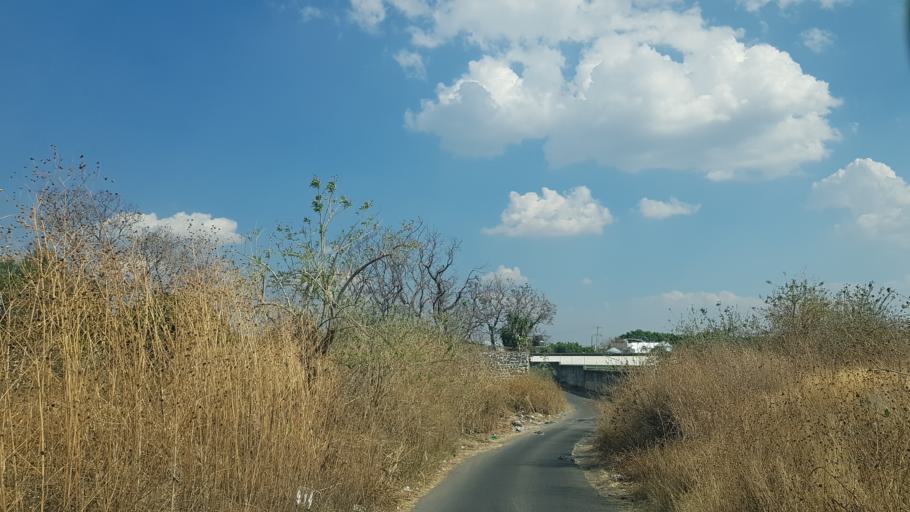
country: MX
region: Puebla
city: Atlixco
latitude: 18.8827
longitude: -98.4908
